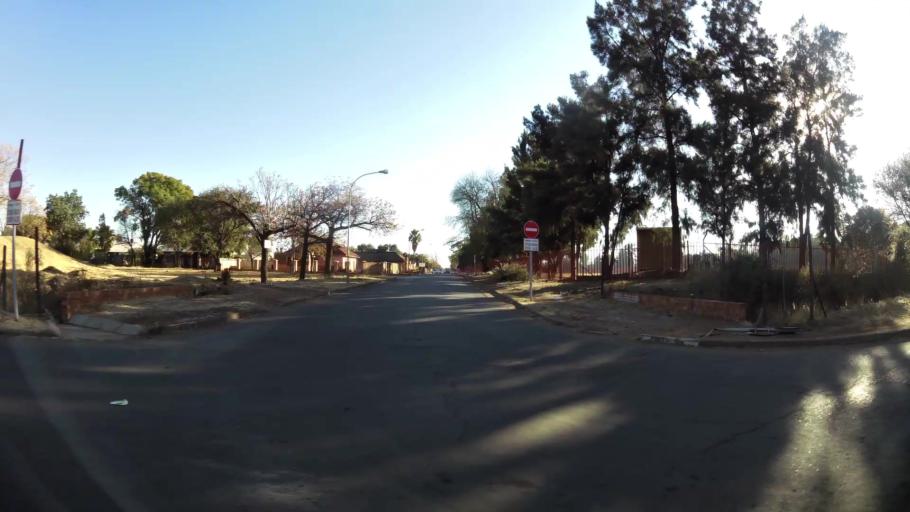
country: ZA
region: Northern Cape
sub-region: Frances Baard District Municipality
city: Kimberley
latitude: -28.7393
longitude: 24.7353
